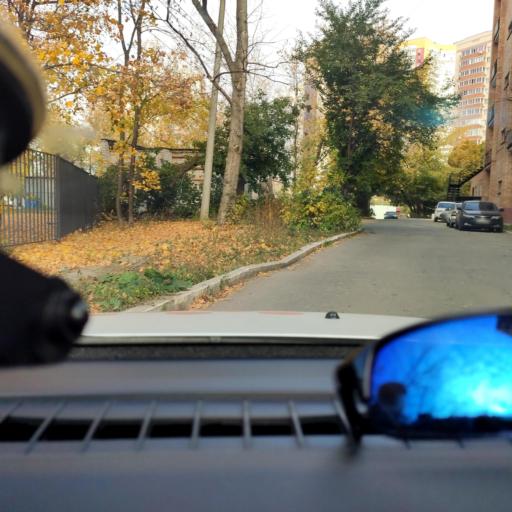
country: RU
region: Samara
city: Samara
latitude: 53.2385
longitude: 50.1864
